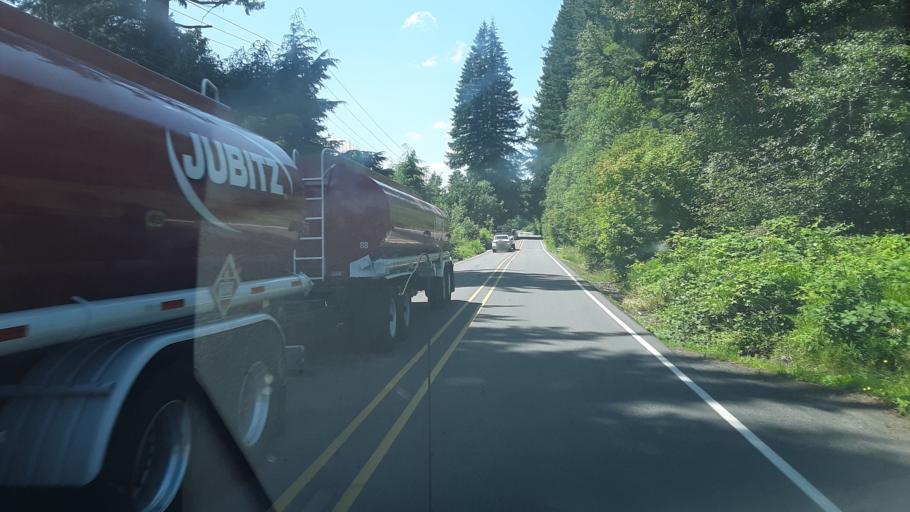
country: US
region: Washington
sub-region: Clark County
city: Yacolt
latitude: 45.9243
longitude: -122.3815
